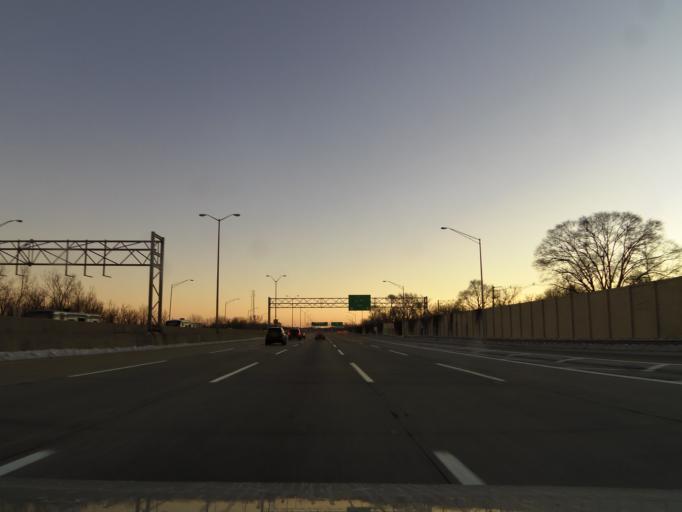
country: US
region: Illinois
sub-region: Cook County
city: University Park
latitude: 41.5971
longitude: -87.6813
